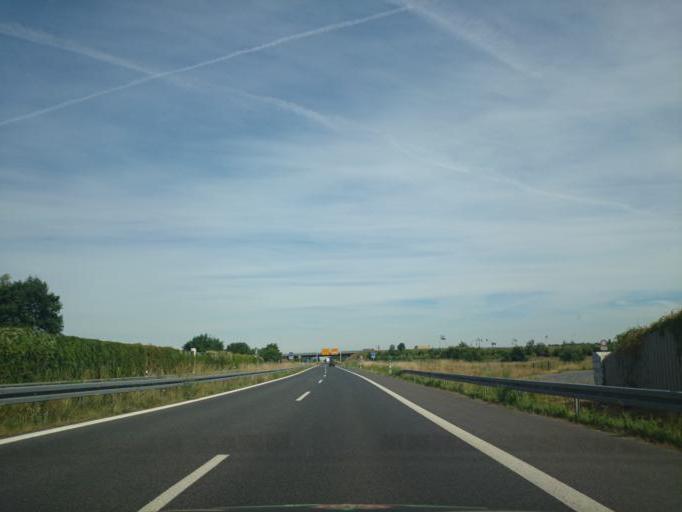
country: DE
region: Berlin
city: Lichtenrade
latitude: 52.3639
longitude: 13.4268
